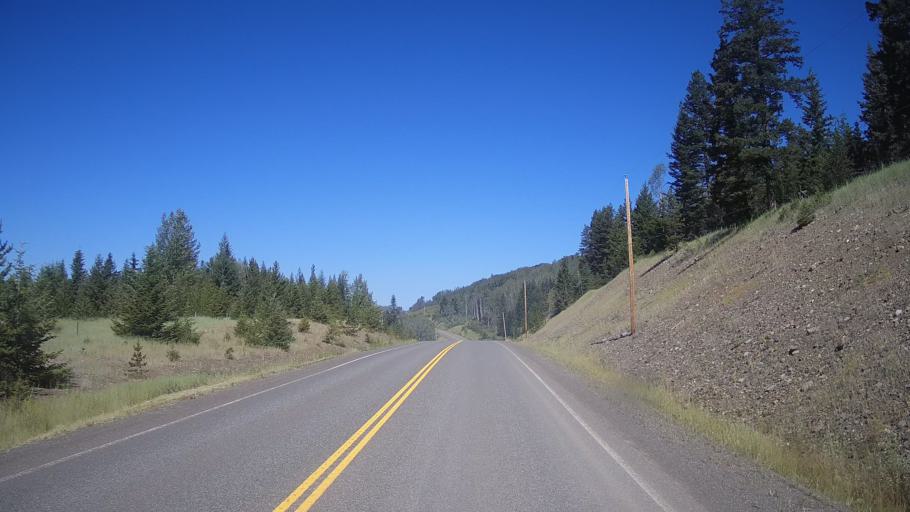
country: CA
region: British Columbia
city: Kamloops
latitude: 51.4937
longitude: -120.5715
